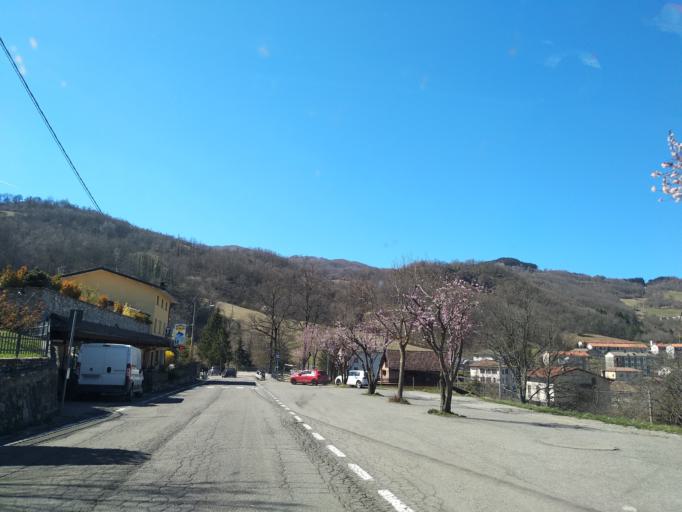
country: IT
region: Emilia-Romagna
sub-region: Provincia di Reggio Emilia
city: Ramiseto
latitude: 44.4123
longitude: 10.2840
